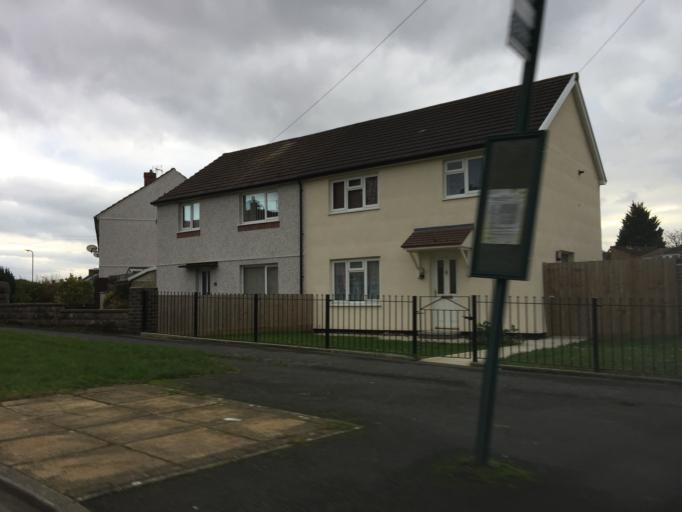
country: GB
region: Wales
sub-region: Monmouthshire
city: Chepstow
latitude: 51.6305
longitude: -2.6801
